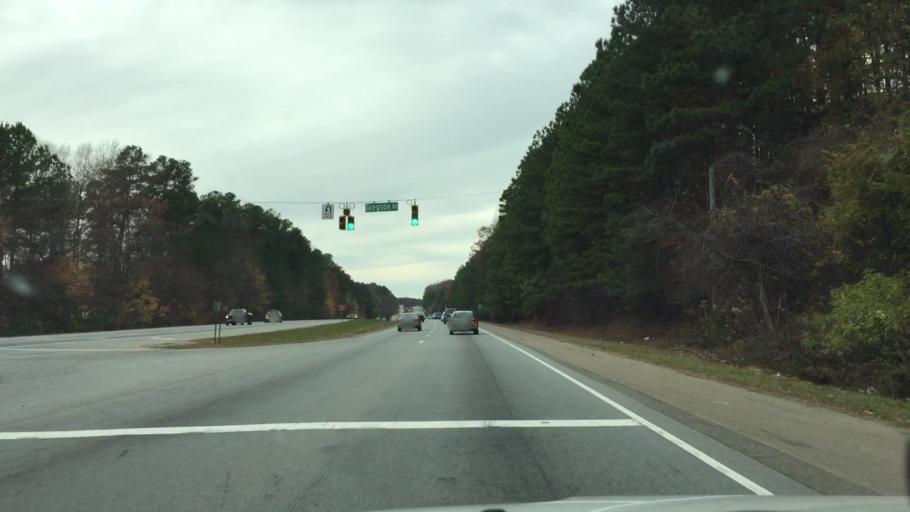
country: US
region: North Carolina
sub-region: Wake County
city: Apex
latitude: 35.7406
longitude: -78.8044
